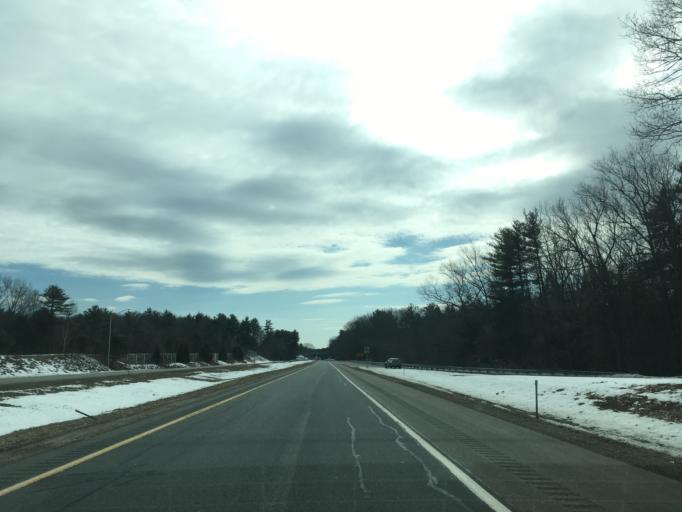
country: US
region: New Hampshire
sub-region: Rockingham County
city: Hampton
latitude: 42.9529
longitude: -70.8527
